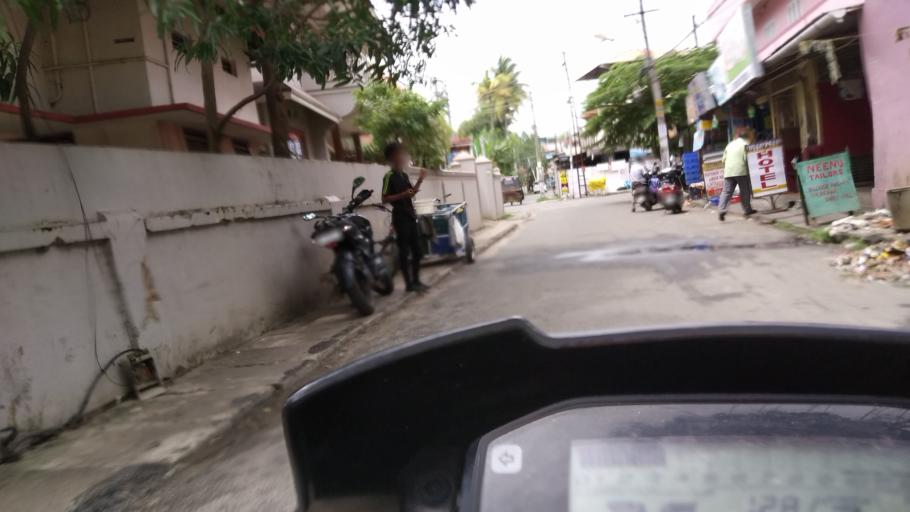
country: IN
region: Kerala
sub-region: Ernakulam
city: Cochin
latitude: 9.9964
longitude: 76.2821
